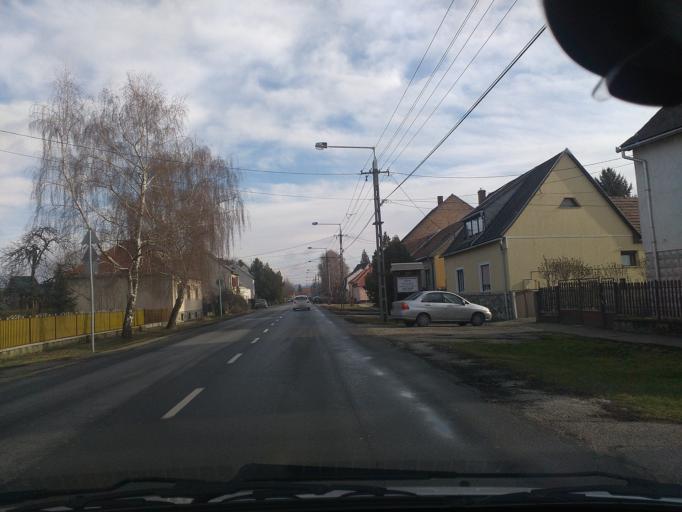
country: HU
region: Komarom-Esztergom
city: Tat
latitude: 47.7486
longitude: 18.6339
